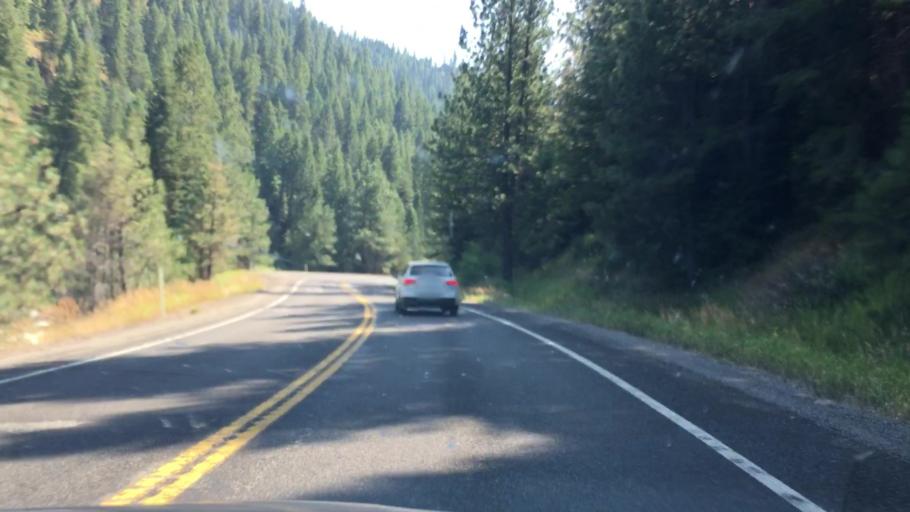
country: US
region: Idaho
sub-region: Valley County
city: Cascade
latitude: 44.2496
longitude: -116.0936
